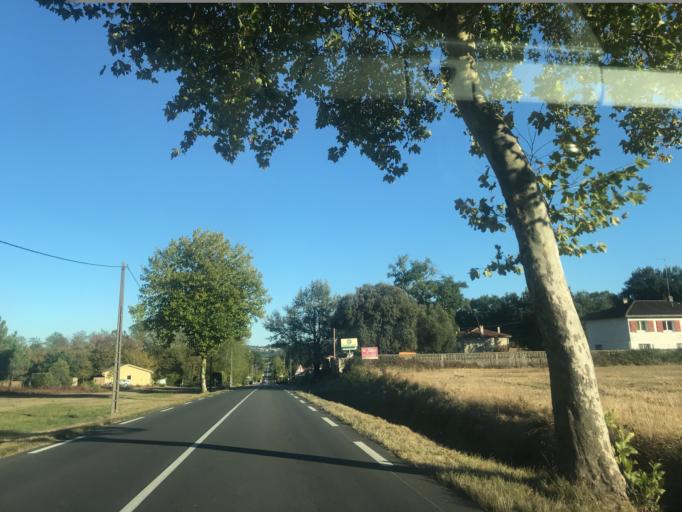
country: FR
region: Poitou-Charentes
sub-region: Departement de la Charente-Maritime
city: Saint-Aigulin
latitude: 45.1641
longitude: -0.0322
